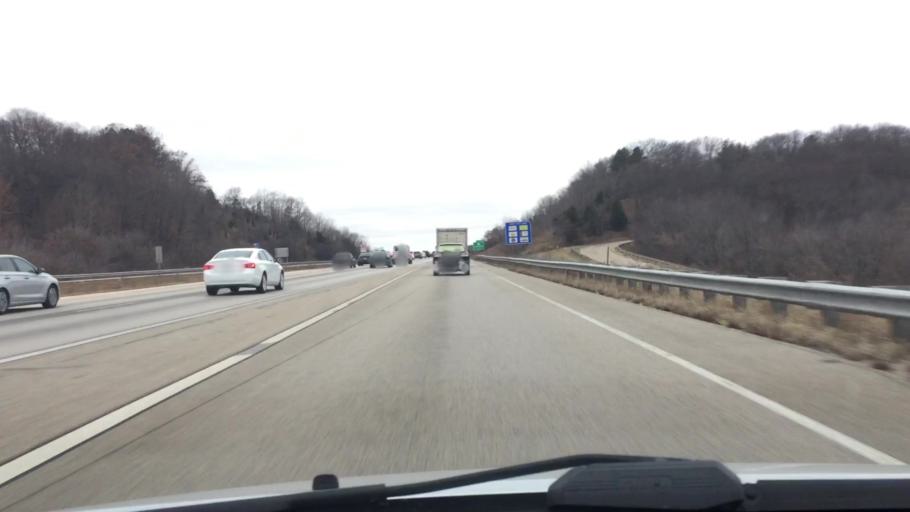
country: US
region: Wisconsin
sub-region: Waukesha County
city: Delafield
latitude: 43.0524
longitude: -88.3793
